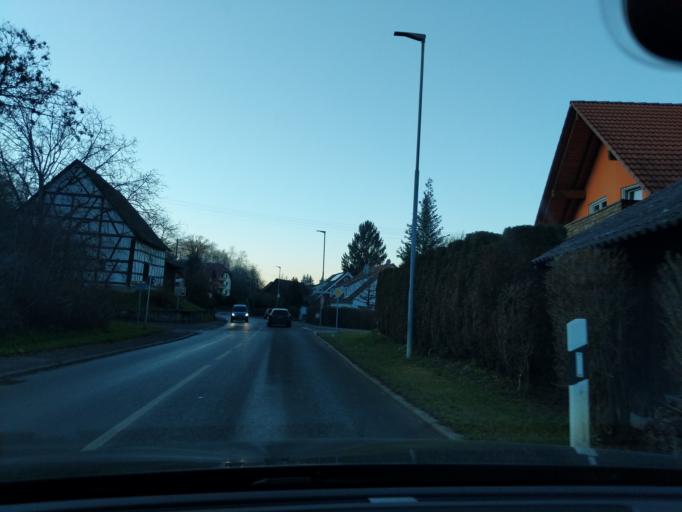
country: DE
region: Baden-Wuerttemberg
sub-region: Tuebingen Region
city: Salem
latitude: 47.7449
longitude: 9.3030
